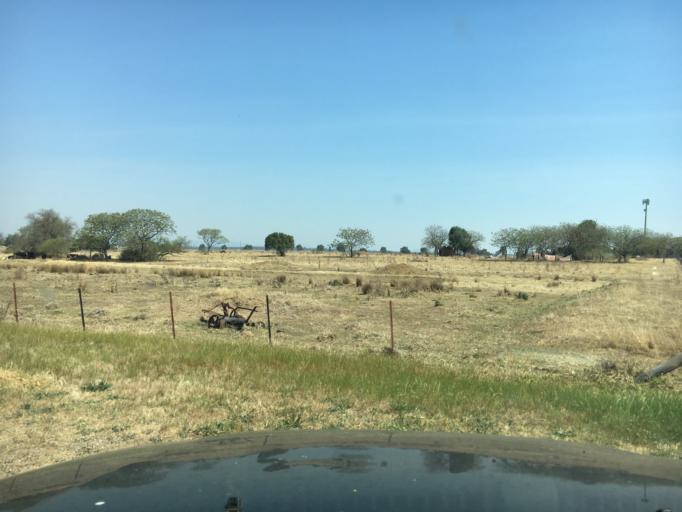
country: AU
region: New South Wales
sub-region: Singleton
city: Singleton
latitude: -32.5682
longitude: 151.1937
